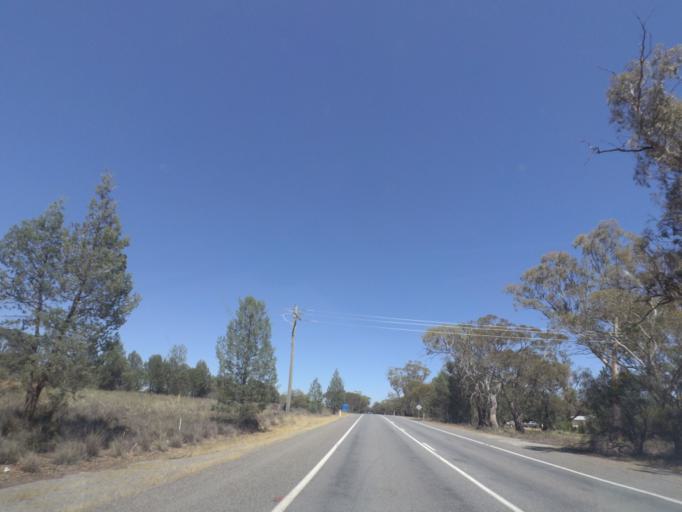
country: AU
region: New South Wales
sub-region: Narrandera
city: Narrandera
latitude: -34.7379
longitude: 146.5820
